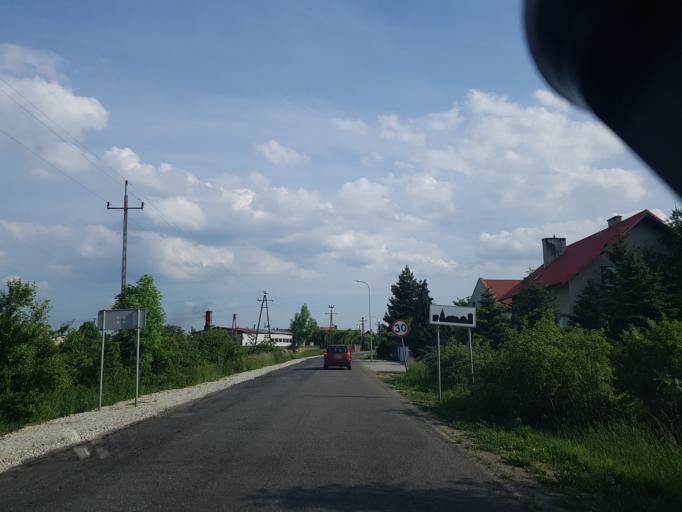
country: PL
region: Lower Silesian Voivodeship
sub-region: Powiat olawski
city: Wierzbno
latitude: 50.8976
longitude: 17.1304
